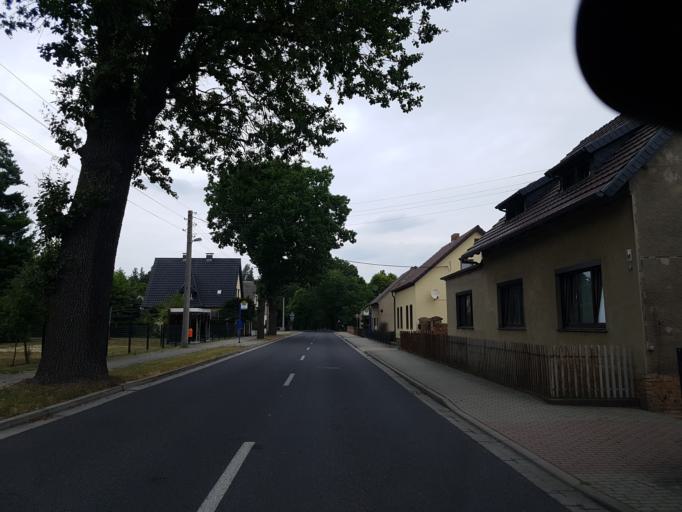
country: DE
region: Brandenburg
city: Sallgast
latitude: 51.5914
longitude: 13.8458
